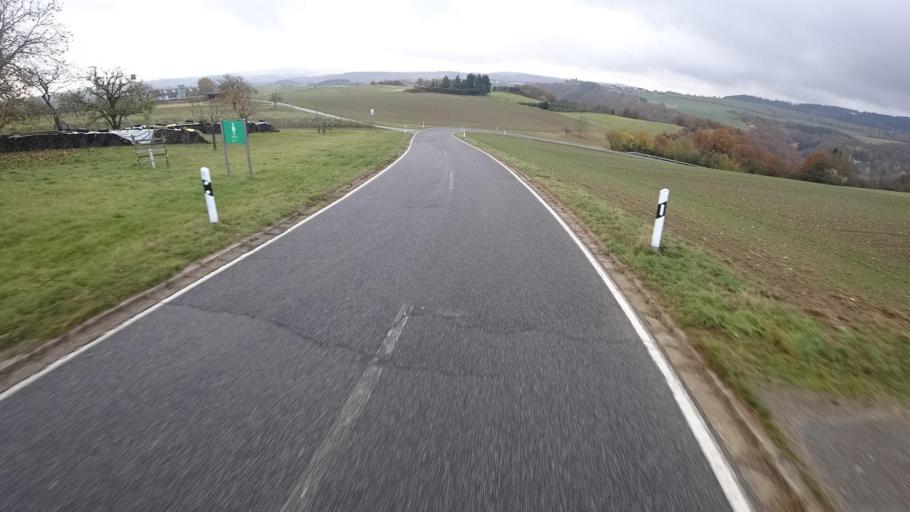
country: DE
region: Rheinland-Pfalz
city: Niederburg
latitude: 50.1164
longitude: 7.6917
